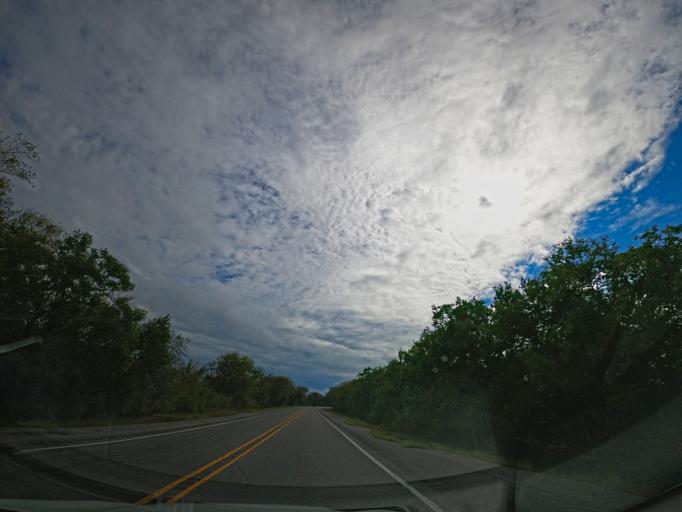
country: US
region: Louisiana
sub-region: Saint Tammany Parish
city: Eden Isle
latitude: 30.0812
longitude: -89.7915
